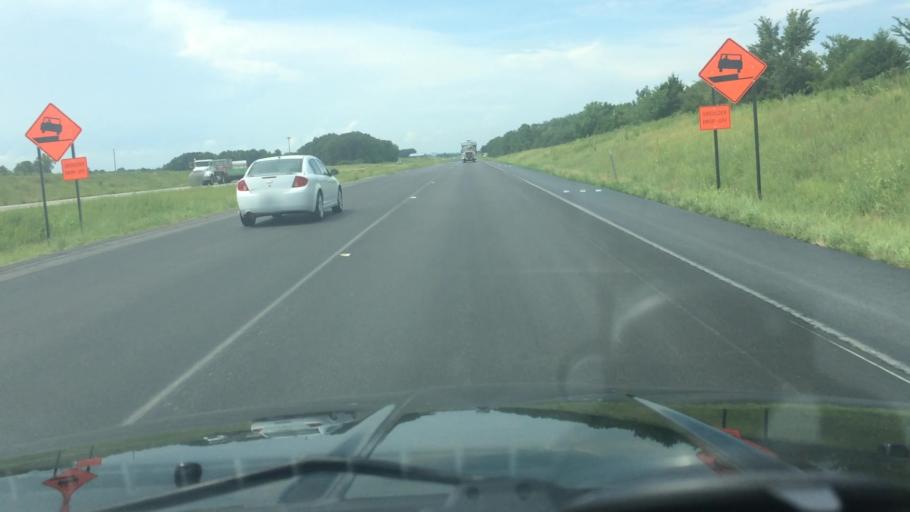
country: US
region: Missouri
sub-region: Saint Clair County
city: Osceola
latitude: 37.9656
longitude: -93.6448
